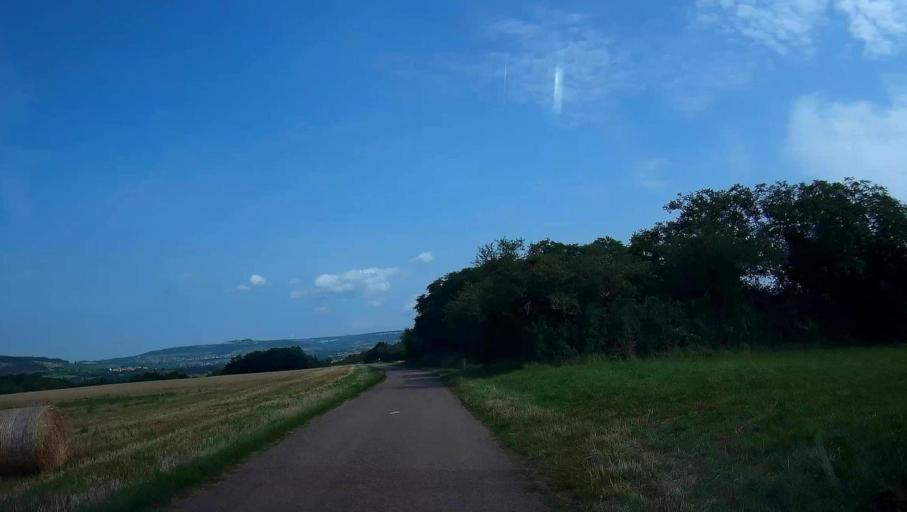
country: FR
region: Bourgogne
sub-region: Departement de la Cote-d'Or
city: Nolay
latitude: 46.9029
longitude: 4.6286
